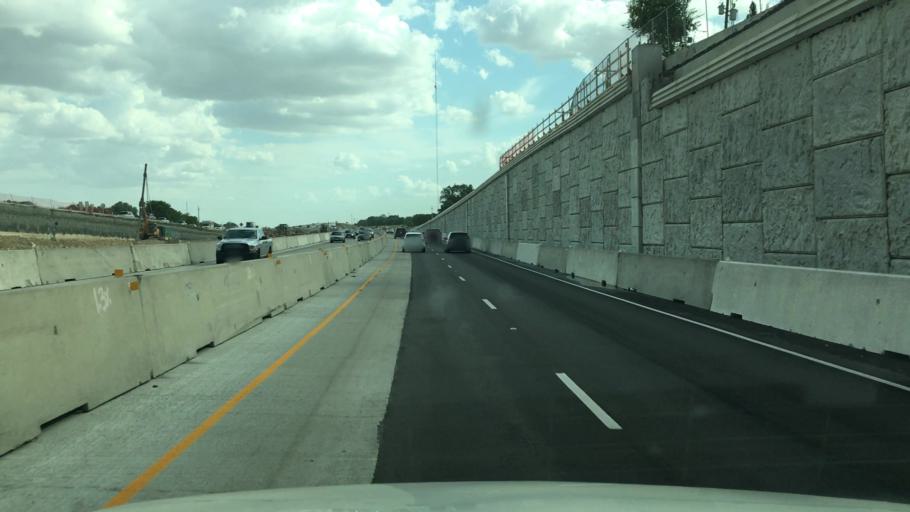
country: US
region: Texas
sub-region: McLennan County
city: Bruceville-Eddy
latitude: 31.2953
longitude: -97.2527
